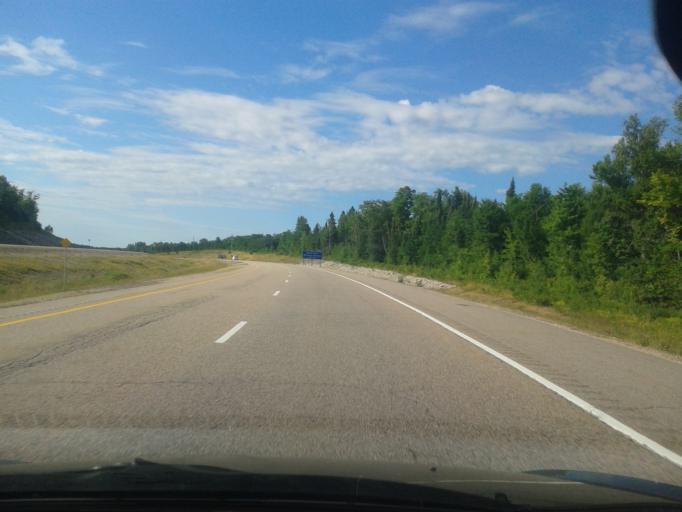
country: CA
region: Ontario
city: South River
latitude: 45.8882
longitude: -79.3805
